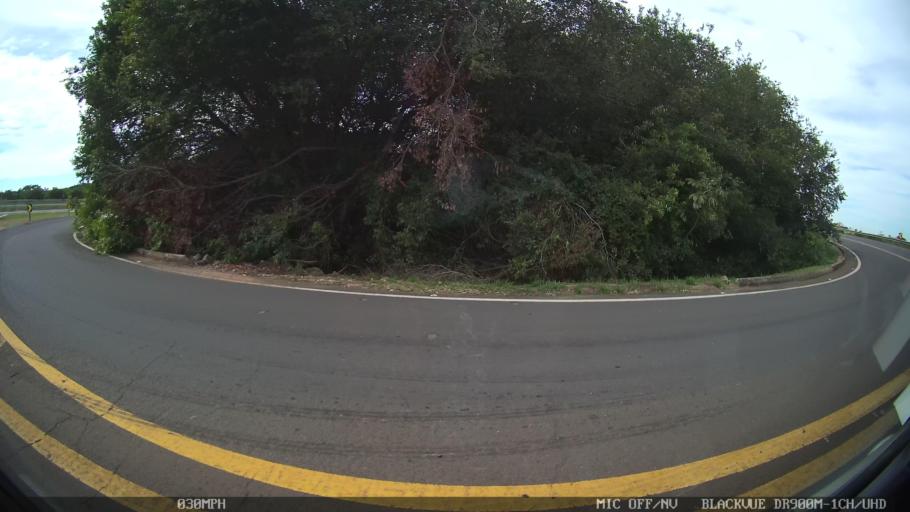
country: BR
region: Sao Paulo
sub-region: Santa Adelia
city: Santa Adelia
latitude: -21.3714
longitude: -48.7505
